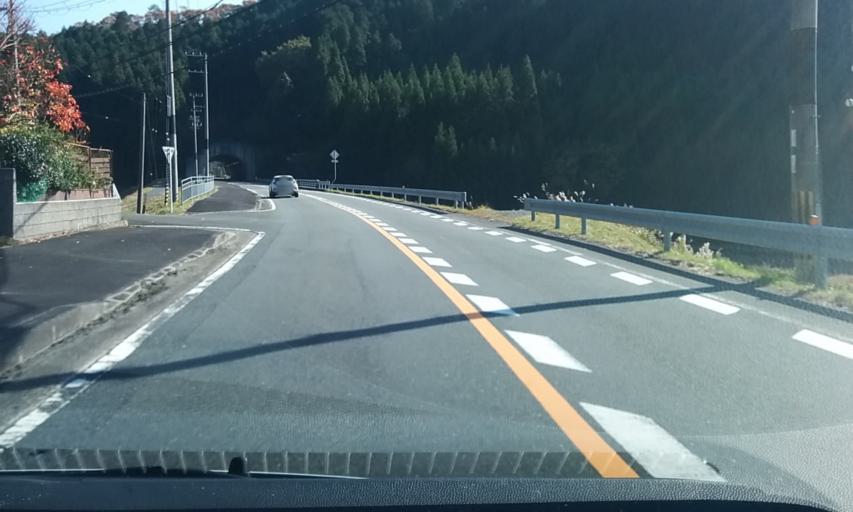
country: JP
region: Kyoto
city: Kameoka
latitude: 35.2128
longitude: 135.5633
